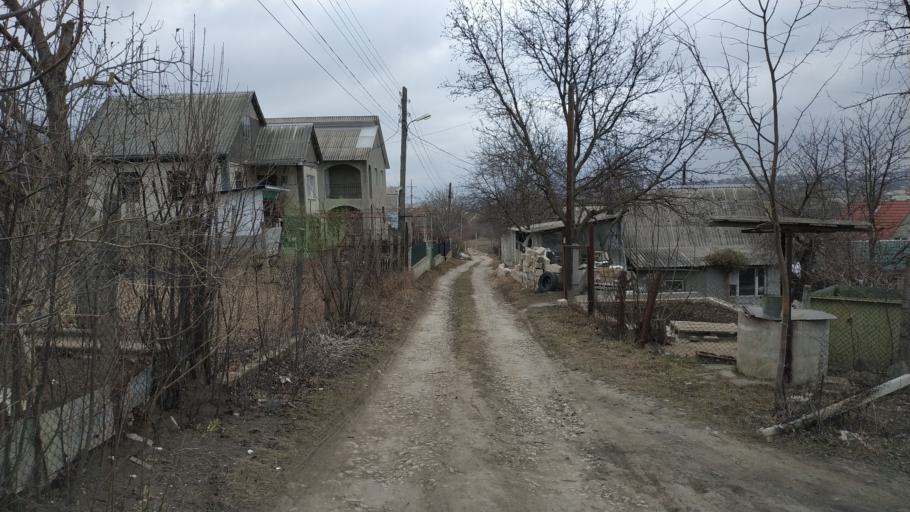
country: MD
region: Laloveni
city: Ialoveni
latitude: 46.9307
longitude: 28.7958
